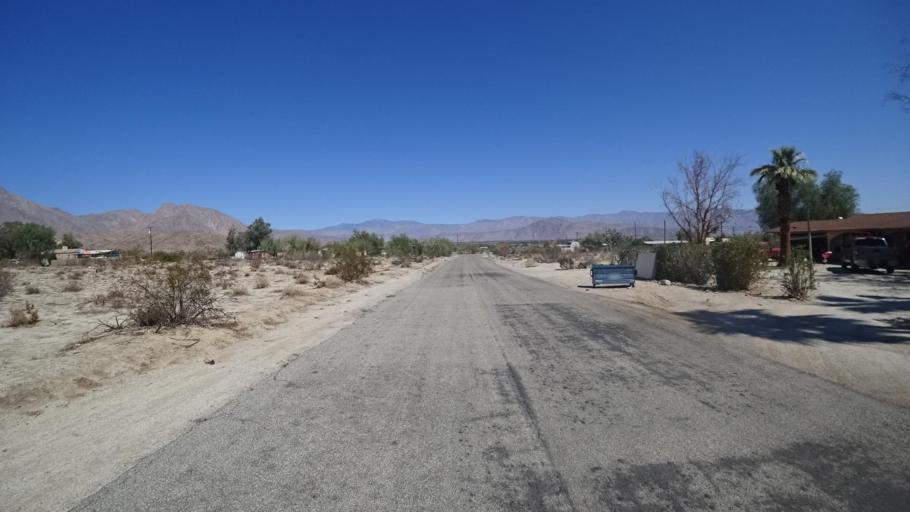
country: US
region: California
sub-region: San Diego County
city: Borrego Springs
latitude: 33.2330
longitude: -116.3739
